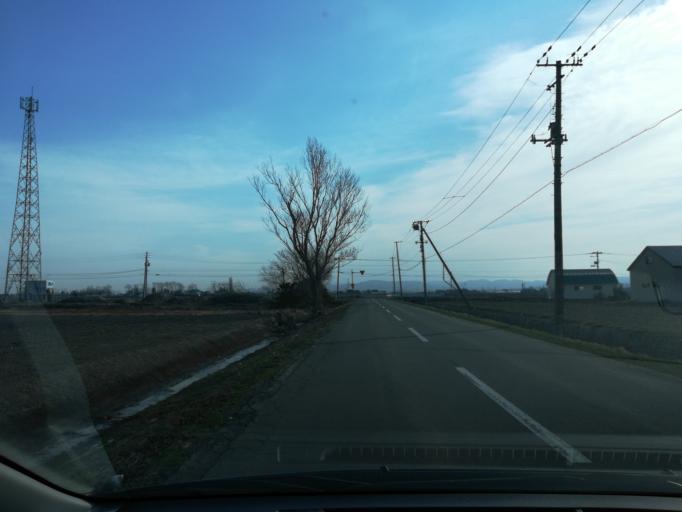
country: JP
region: Hokkaido
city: Iwamizawa
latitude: 43.1947
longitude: 141.7155
